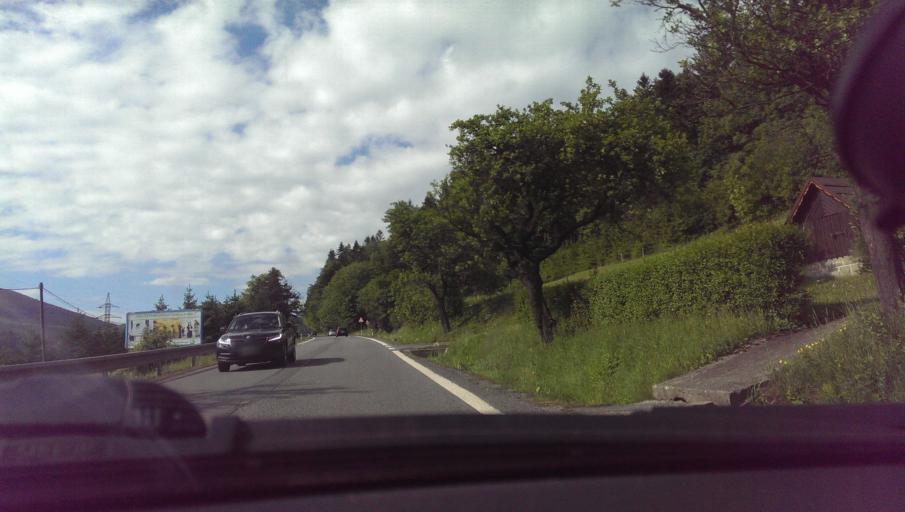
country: CZ
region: Moravskoslezsky
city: Frenstat pod Radhostem
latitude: 49.5124
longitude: 18.1958
